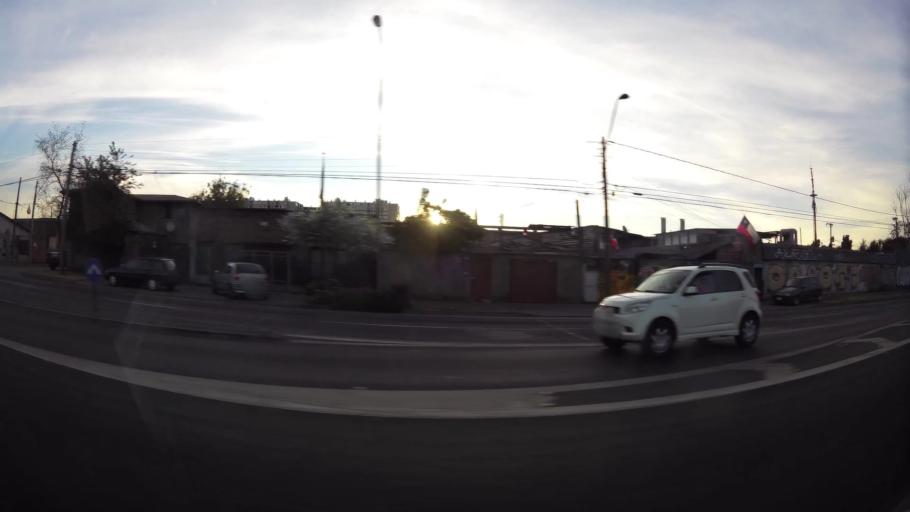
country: CL
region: Santiago Metropolitan
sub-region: Provincia de Santiago
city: Lo Prado
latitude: -33.4427
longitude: -70.6920
